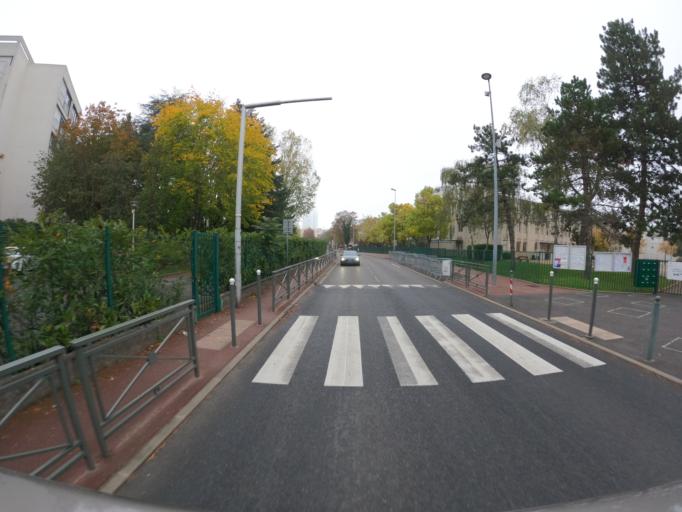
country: FR
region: Ile-de-France
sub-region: Departement du Val-de-Marne
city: Chennevieres-sur-Marne
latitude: 48.7996
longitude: 2.5534
